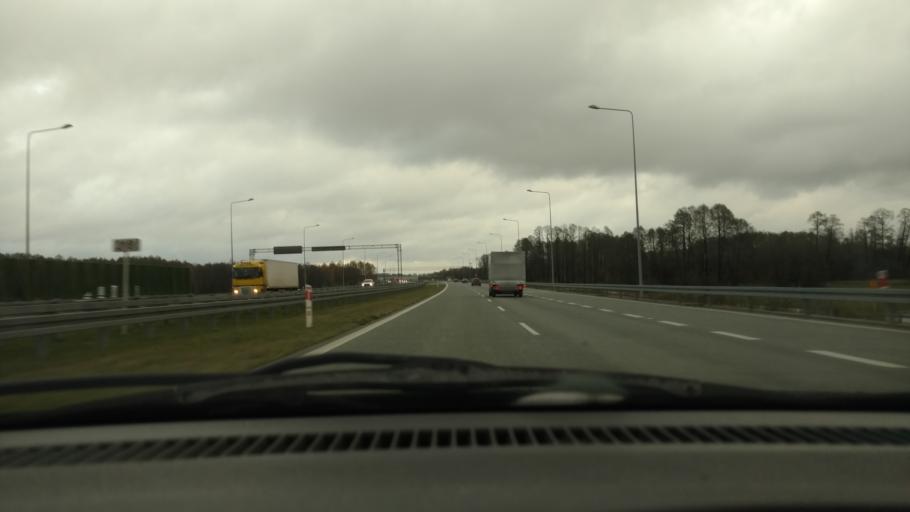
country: PL
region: Lodz Voivodeship
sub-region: Powiat pabianicki
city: Pabianice
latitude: 51.6149
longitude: 19.3696
